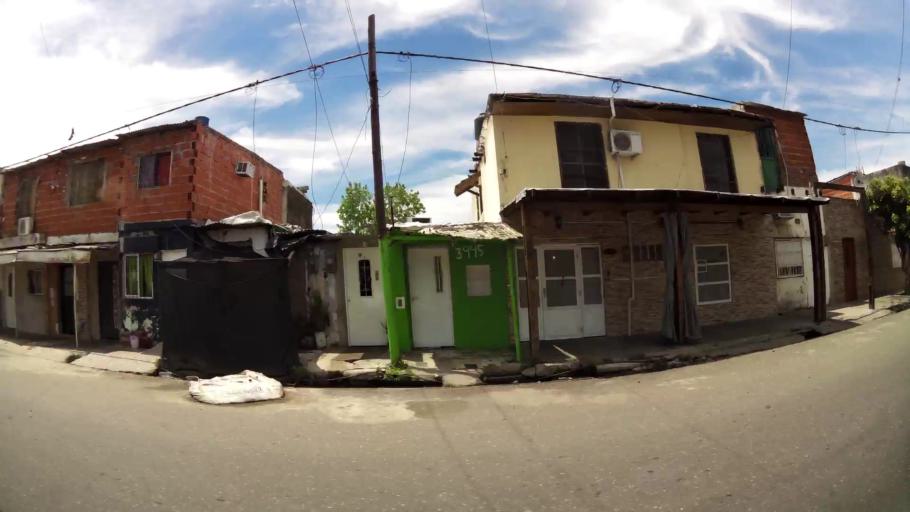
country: AR
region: Santa Fe
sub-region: Departamento de Rosario
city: Rosario
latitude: -32.9849
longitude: -60.6361
